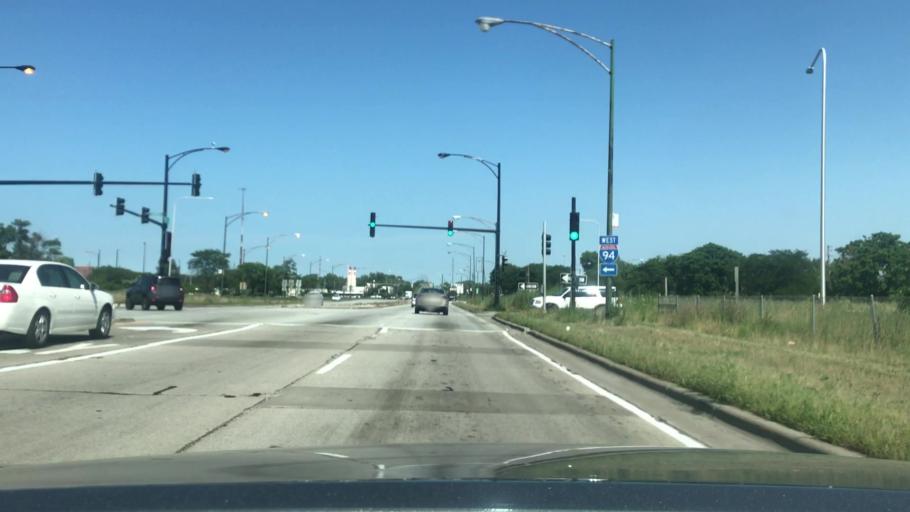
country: US
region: Illinois
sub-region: Cook County
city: Dolton
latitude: 41.7077
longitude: -87.5851
